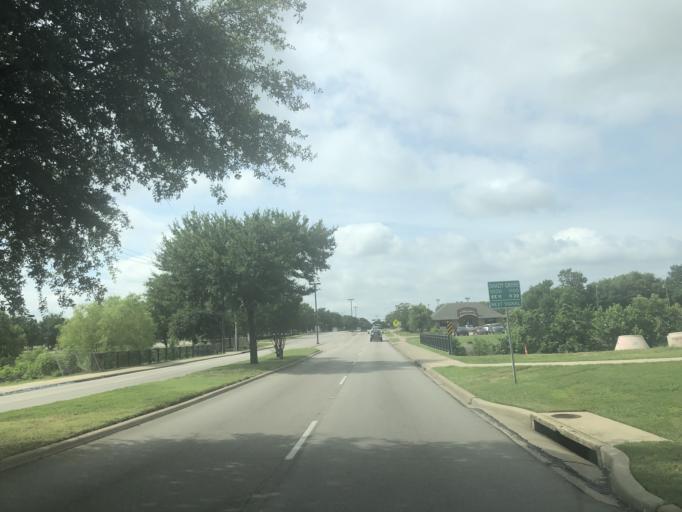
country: US
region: Texas
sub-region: Dallas County
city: Irving
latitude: 32.8038
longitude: -96.9594
